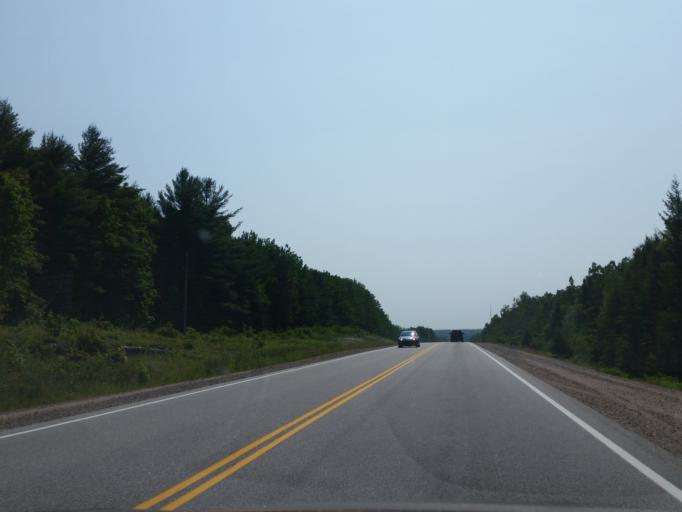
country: CA
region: Ontario
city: Mattawa
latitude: 46.2982
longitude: -78.5529
